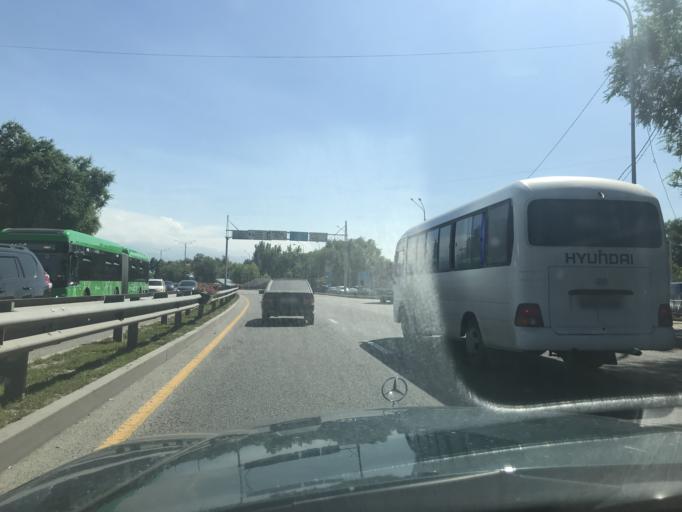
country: KZ
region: Almaty Qalasy
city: Almaty
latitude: 43.2883
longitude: 76.9886
